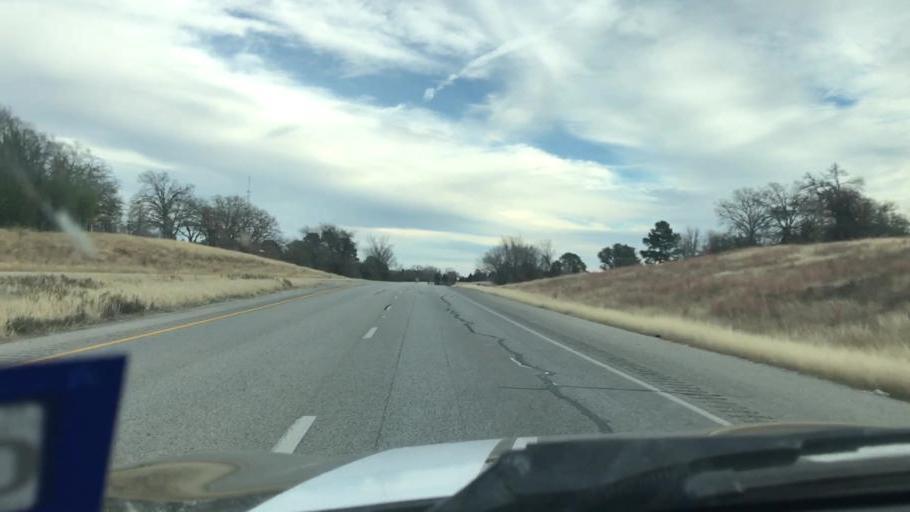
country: US
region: Texas
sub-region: Bastrop County
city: Elgin
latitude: 30.3026
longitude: -97.2937
